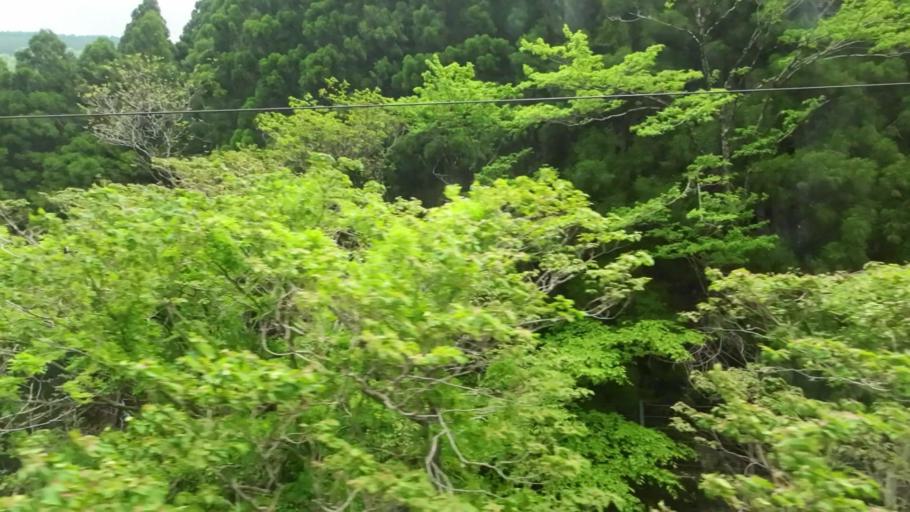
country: JP
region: Tokushima
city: Ikedacho
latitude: 33.9094
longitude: 133.7575
